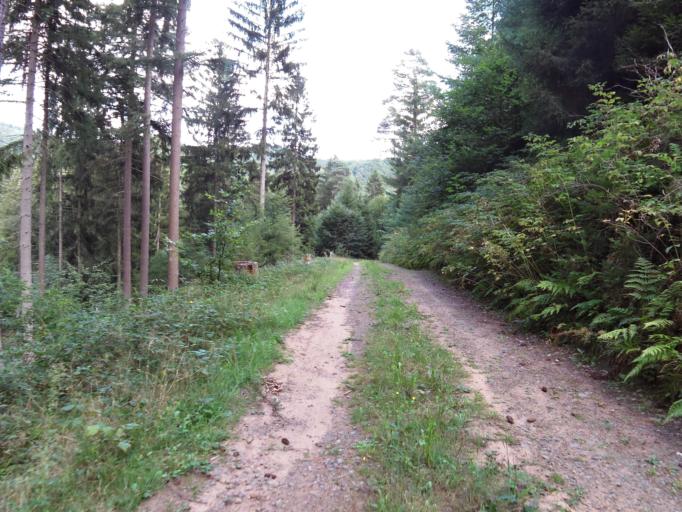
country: DE
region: Rheinland-Pfalz
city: Frankenstein
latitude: 49.4622
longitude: 8.0183
